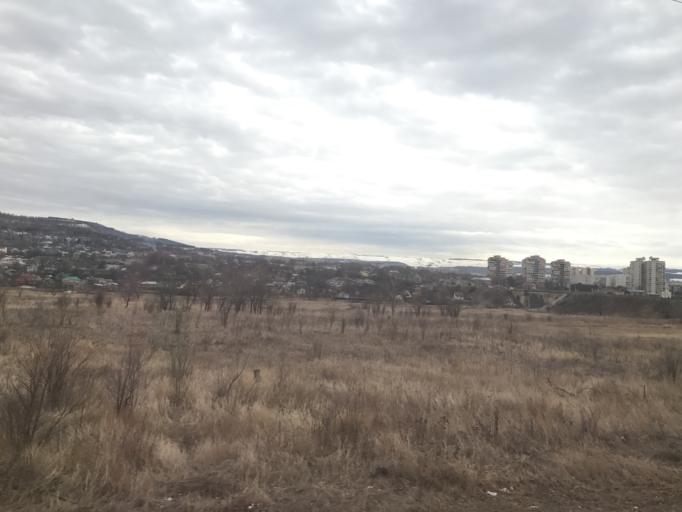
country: RU
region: Stavropol'skiy
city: Kislovodsk
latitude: 43.9470
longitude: 42.7343
